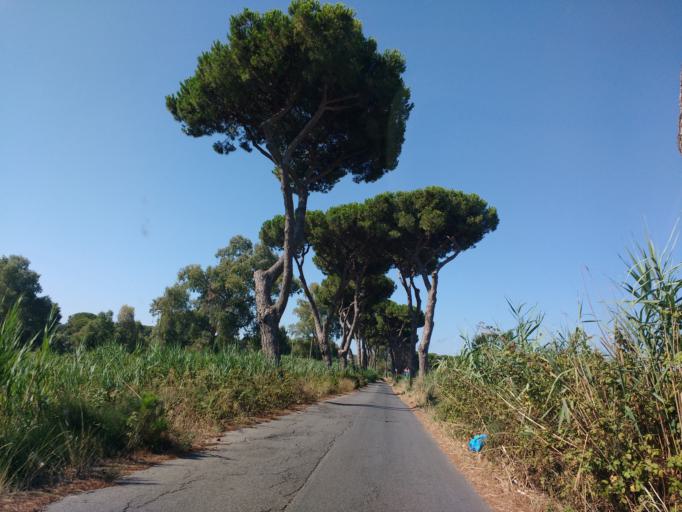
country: IT
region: Latium
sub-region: Citta metropolitana di Roma Capitale
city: Acilia-Castel Fusano-Ostia Antica
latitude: 41.7471
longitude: 12.3241
